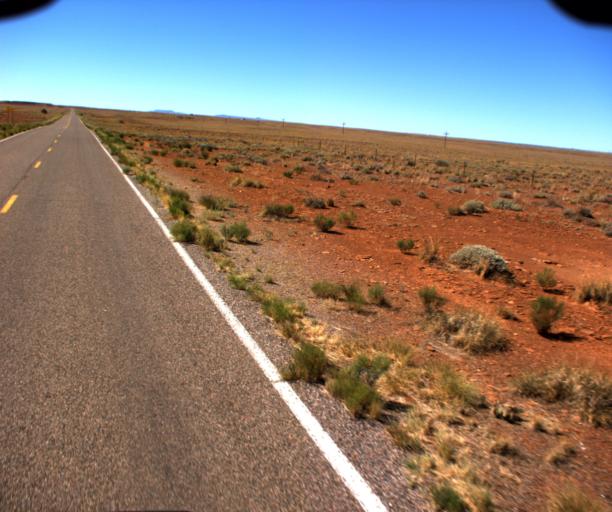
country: US
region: Arizona
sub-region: Coconino County
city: LeChee
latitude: 35.2209
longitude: -110.9532
